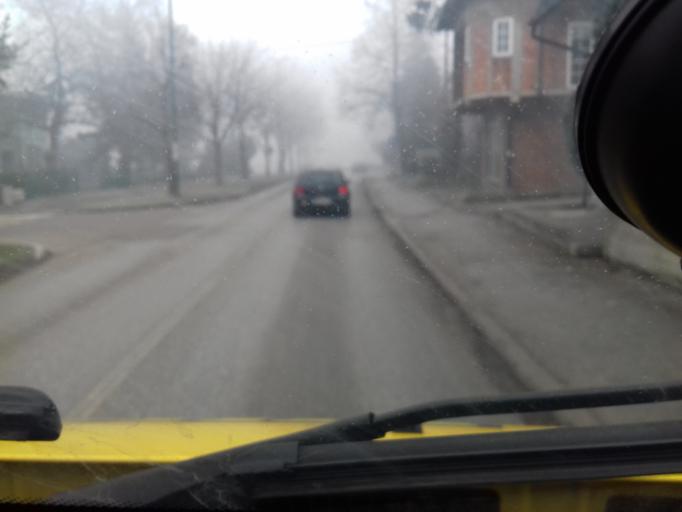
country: BA
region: Federation of Bosnia and Herzegovina
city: Visoko
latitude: 43.9947
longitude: 18.1731
